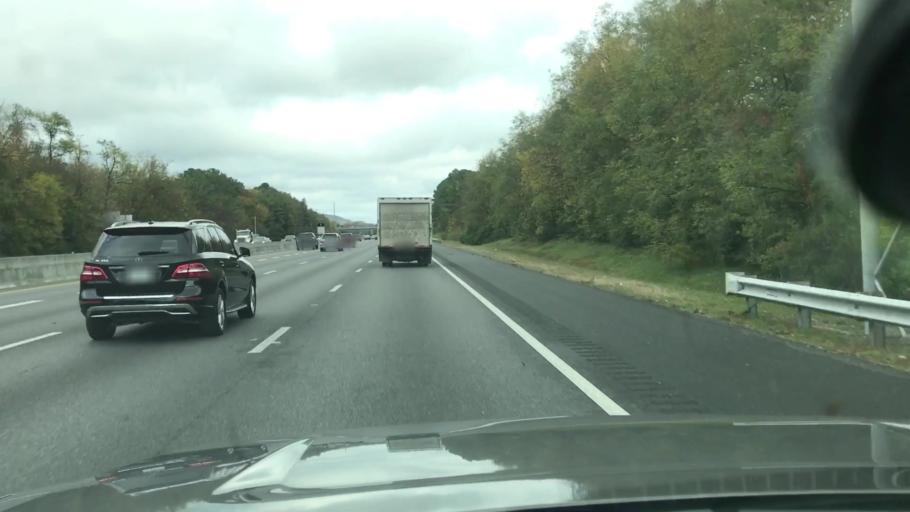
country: US
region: Tennessee
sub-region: Williamson County
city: Brentwood Estates
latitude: 35.9919
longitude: -86.7986
